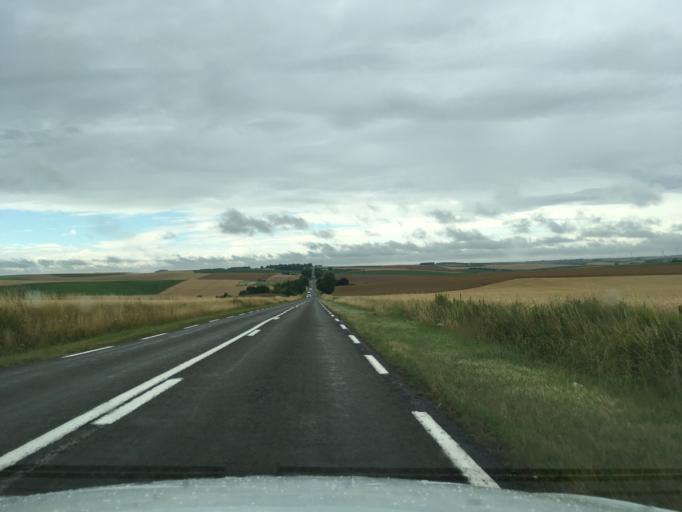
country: FR
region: Picardie
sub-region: Departement de l'Aisne
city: Guise
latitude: 49.8824
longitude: 3.6024
